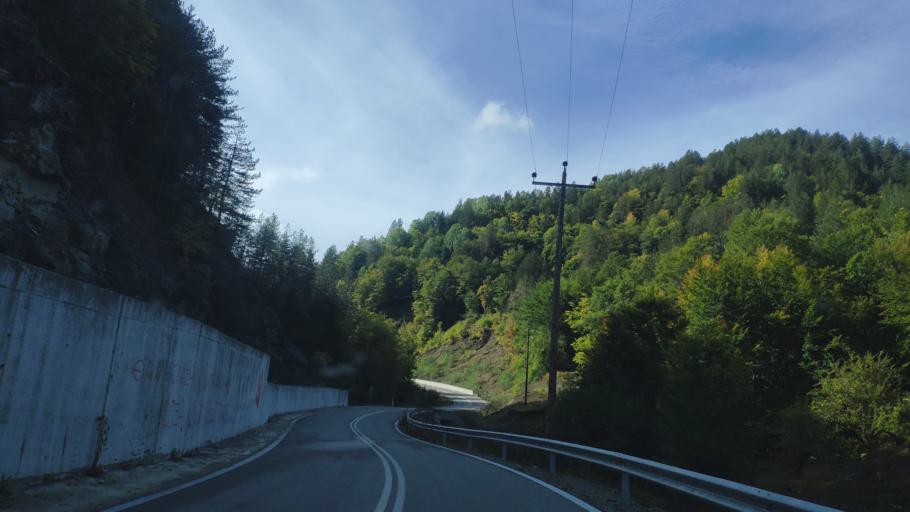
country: GR
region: West Macedonia
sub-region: Nomos Kastorias
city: Nestorio
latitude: 40.3805
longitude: 20.9420
